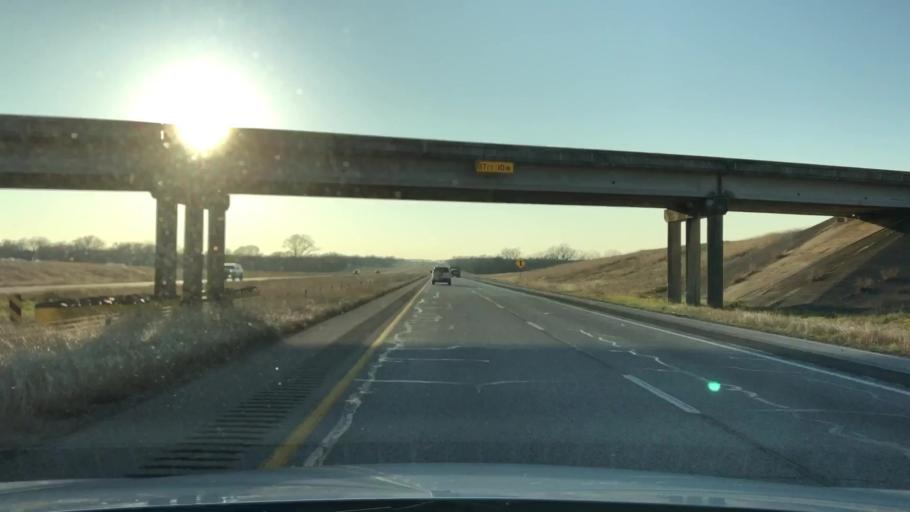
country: US
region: Texas
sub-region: Caldwell County
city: Luling
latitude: 29.6451
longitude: -97.6975
